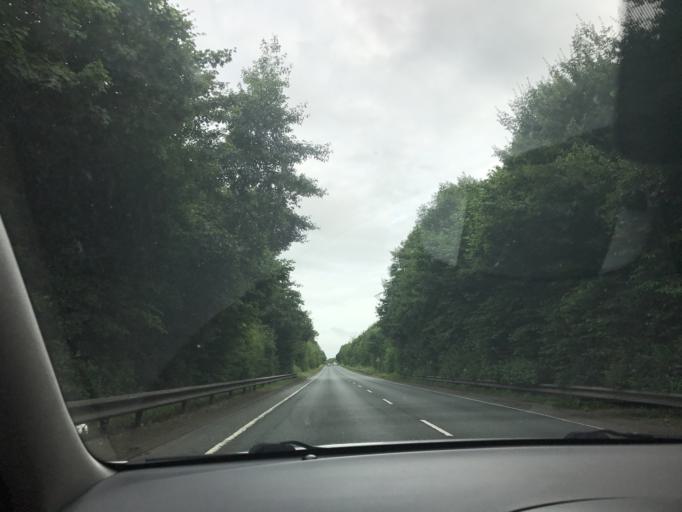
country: GB
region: England
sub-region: Cheshire West and Chester
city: Northwich
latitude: 53.2373
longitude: -2.5028
